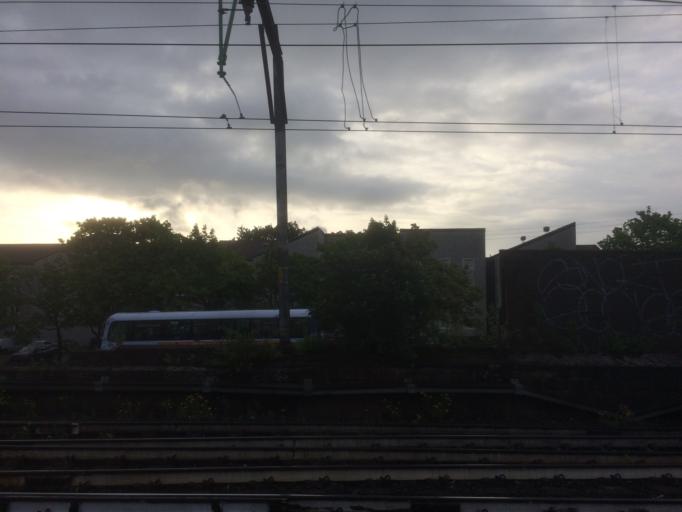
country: GB
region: Scotland
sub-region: Glasgow City
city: Glasgow
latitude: 55.8498
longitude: -4.2606
